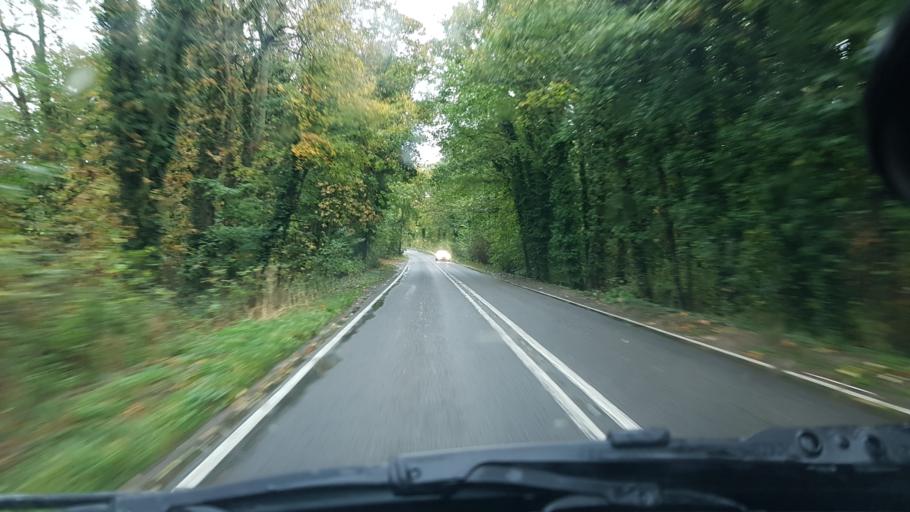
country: GB
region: England
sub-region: Oxfordshire
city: Ducklington
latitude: 51.7582
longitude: -1.4643
